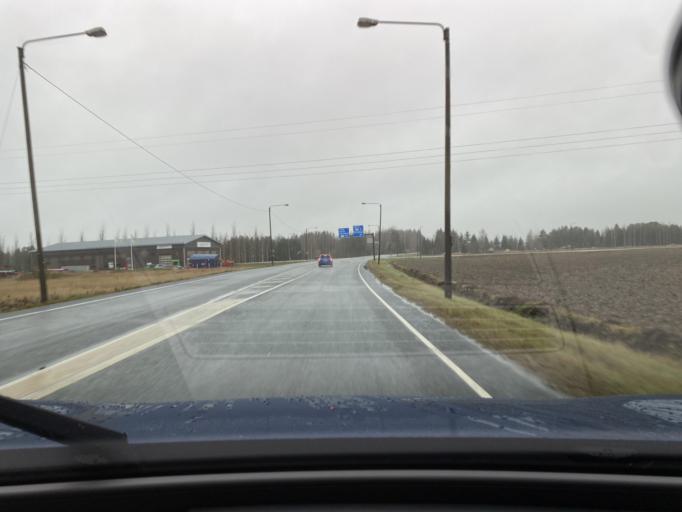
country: FI
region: Varsinais-Suomi
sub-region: Loimaa
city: Loimaa
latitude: 60.8684
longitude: 23.0060
